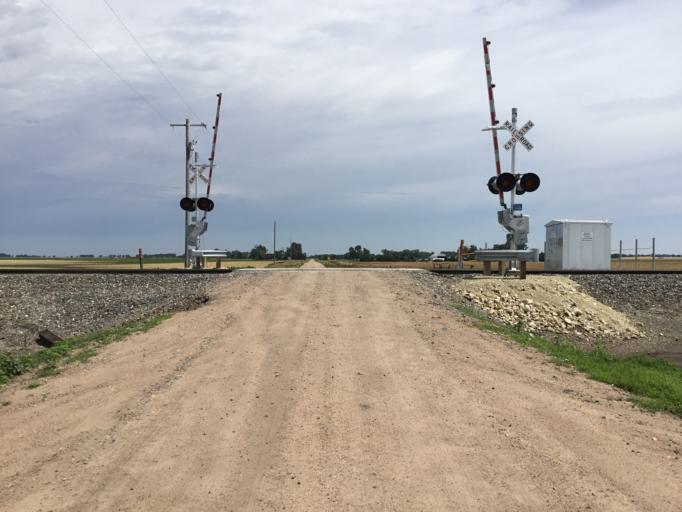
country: US
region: Kansas
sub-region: Reno County
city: Nickerson
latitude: 37.9705
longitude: -98.1421
